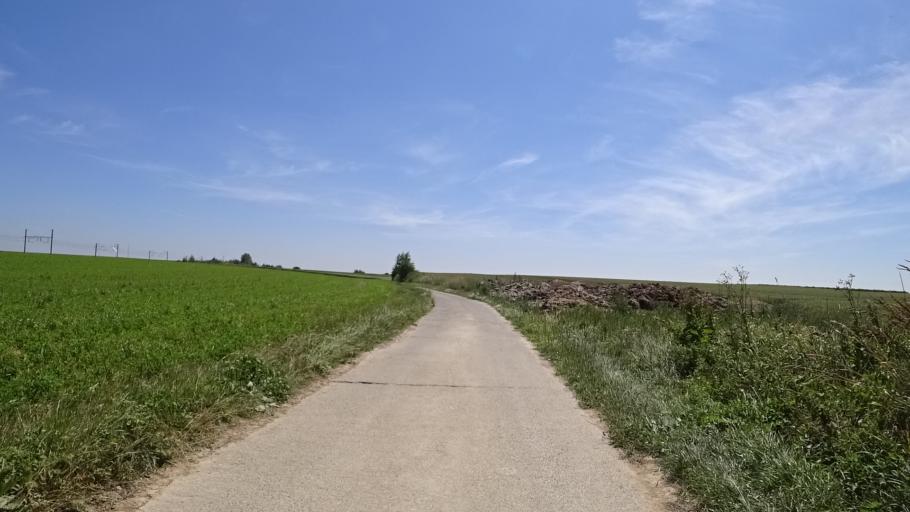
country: BE
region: Wallonia
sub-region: Province de Namur
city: Gembloux
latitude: 50.5836
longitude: 4.6749
